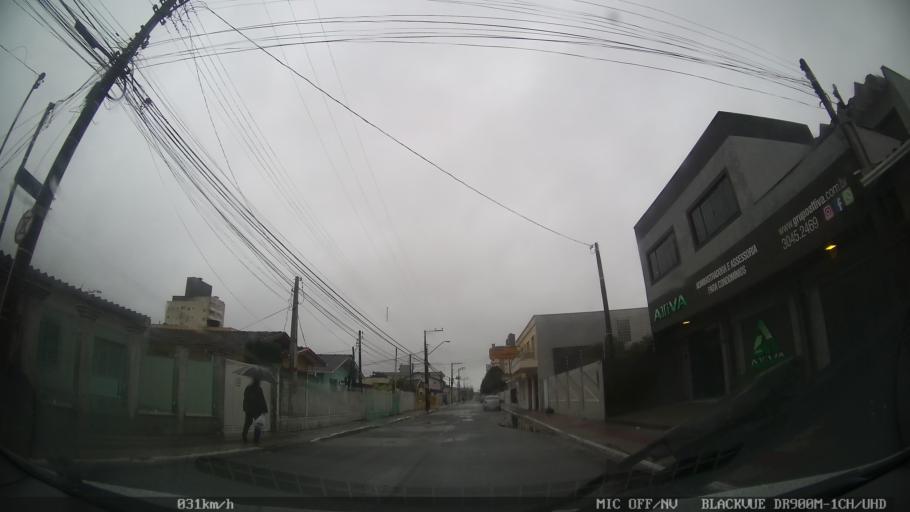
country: BR
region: Santa Catarina
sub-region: Itajai
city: Itajai
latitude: -26.9010
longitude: -48.6768
